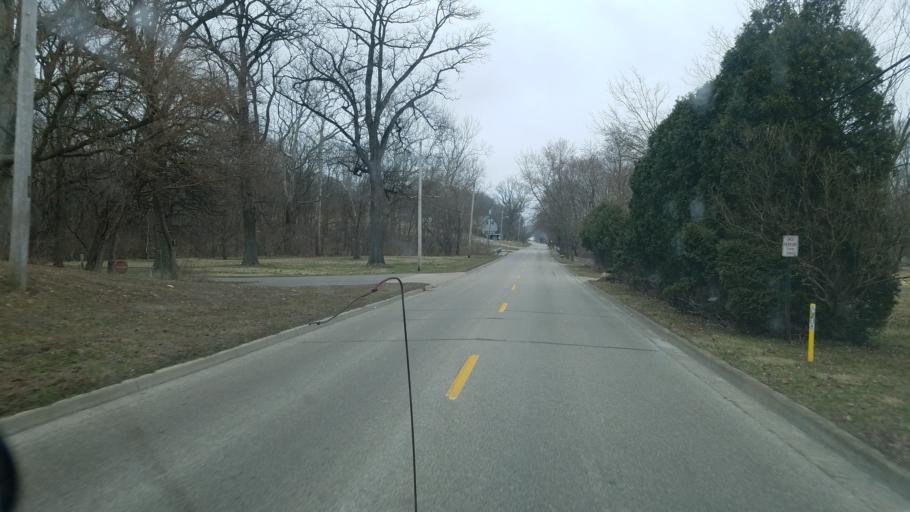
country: US
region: Indiana
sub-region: Wabash County
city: Wabash
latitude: 40.7979
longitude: -85.8411
